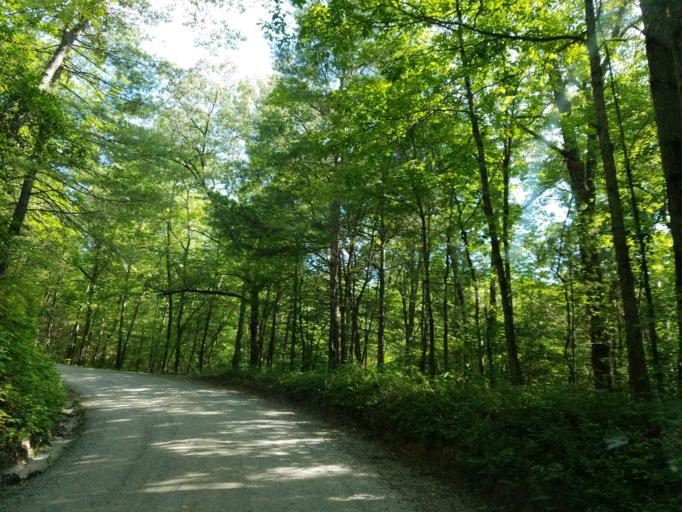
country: US
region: Georgia
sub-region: Fannin County
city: Blue Ridge
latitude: 34.7980
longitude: -84.2435
